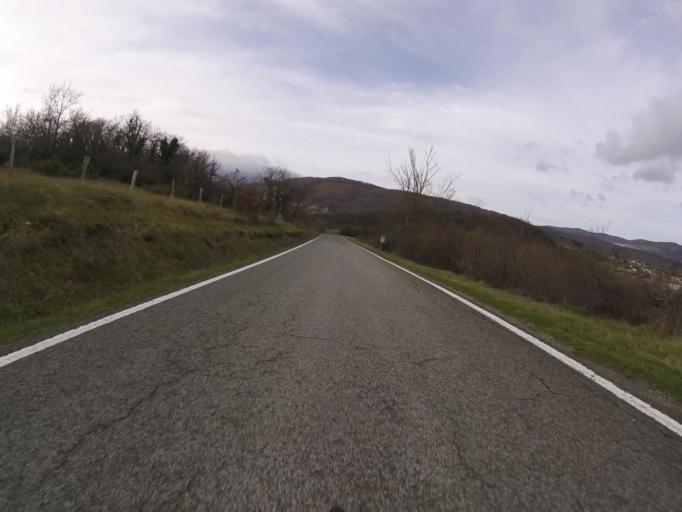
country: ES
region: Navarre
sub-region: Provincia de Navarra
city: Olazagutia
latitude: 42.8797
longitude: -2.1793
